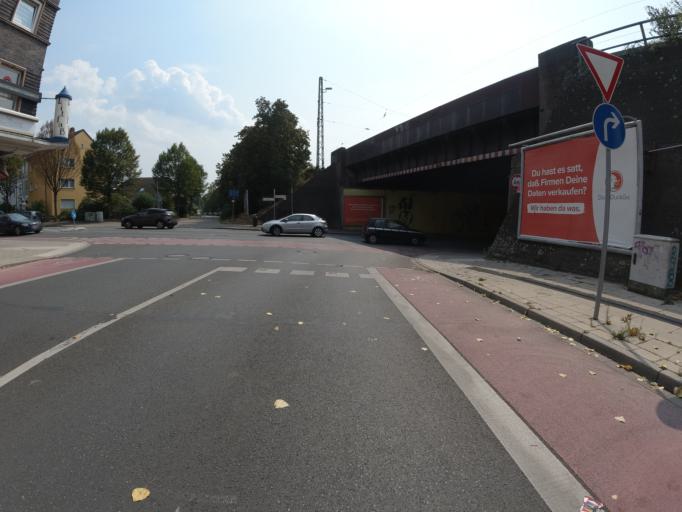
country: DE
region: North Rhine-Westphalia
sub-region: Regierungsbezirk Dusseldorf
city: Moers
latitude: 51.4502
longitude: 6.6424
